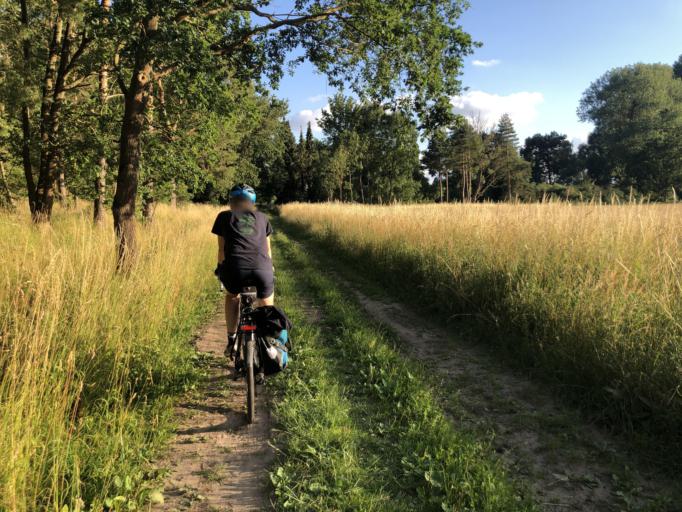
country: DE
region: Lower Saxony
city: Tosterglope
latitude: 53.2541
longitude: 10.7896
